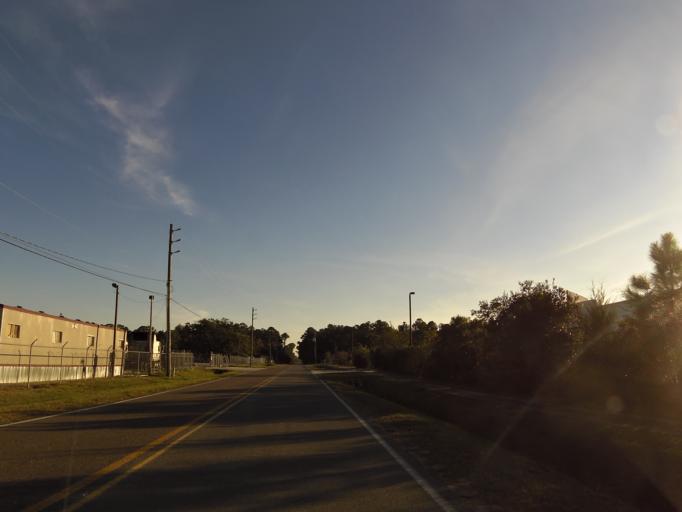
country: US
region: Florida
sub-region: Duval County
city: Jacksonville
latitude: 30.3518
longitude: -81.7647
